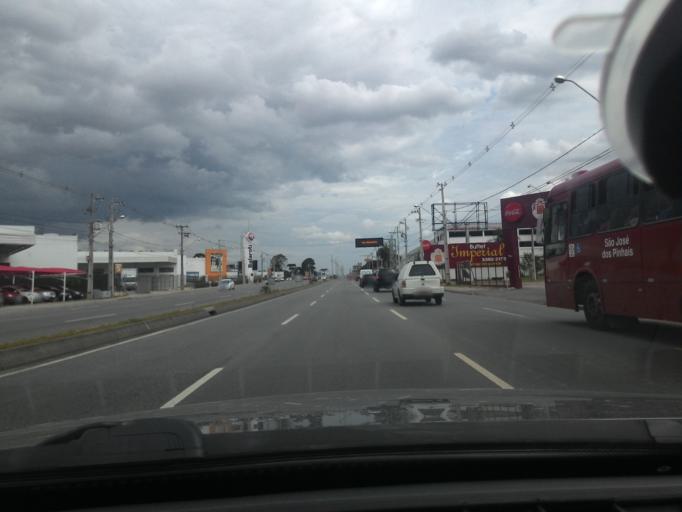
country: BR
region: Parana
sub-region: Sao Jose Dos Pinhais
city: Sao Jose dos Pinhais
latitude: -25.5274
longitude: -49.1968
